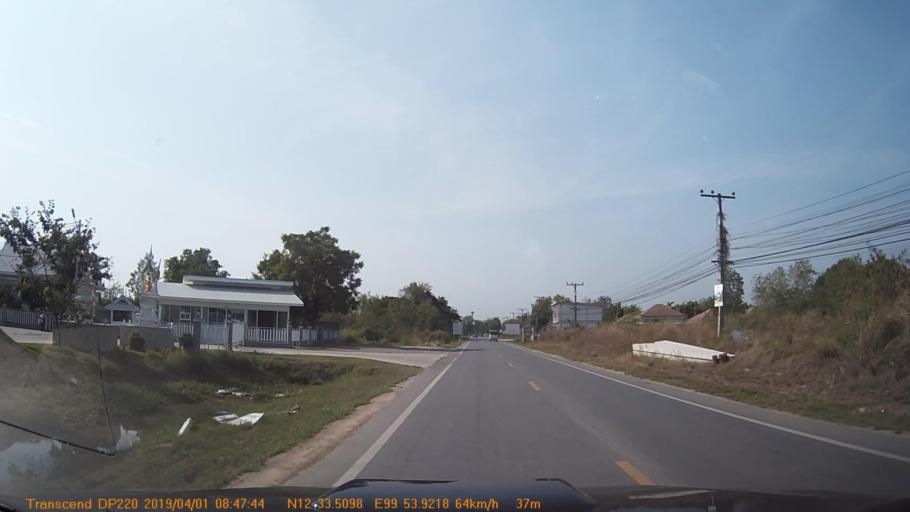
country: TH
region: Prachuap Khiri Khan
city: Hua Hin
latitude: 12.5583
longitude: 99.8987
